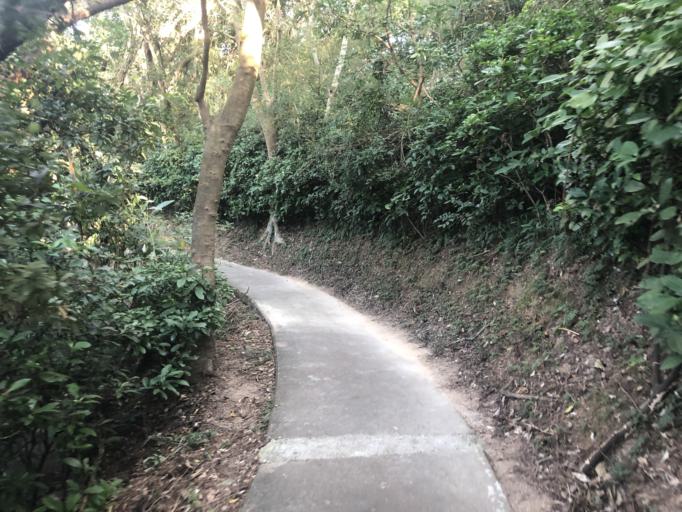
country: HK
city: Yung Shue Wan
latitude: 22.2150
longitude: 114.0276
